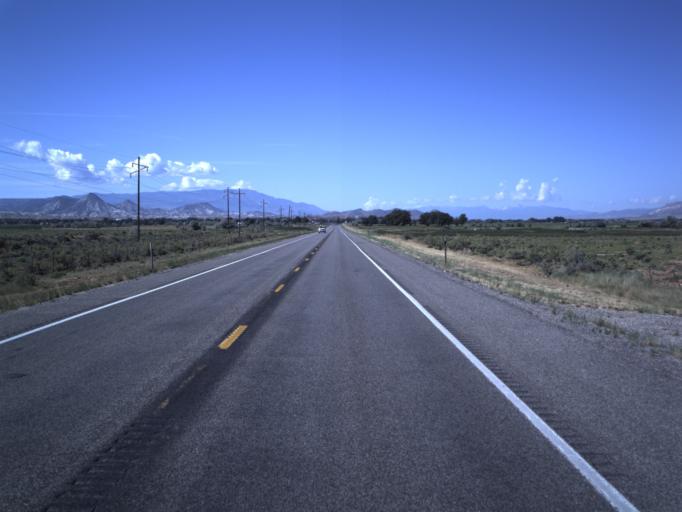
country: US
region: Utah
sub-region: Sevier County
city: Salina
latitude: 38.9935
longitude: -111.8456
